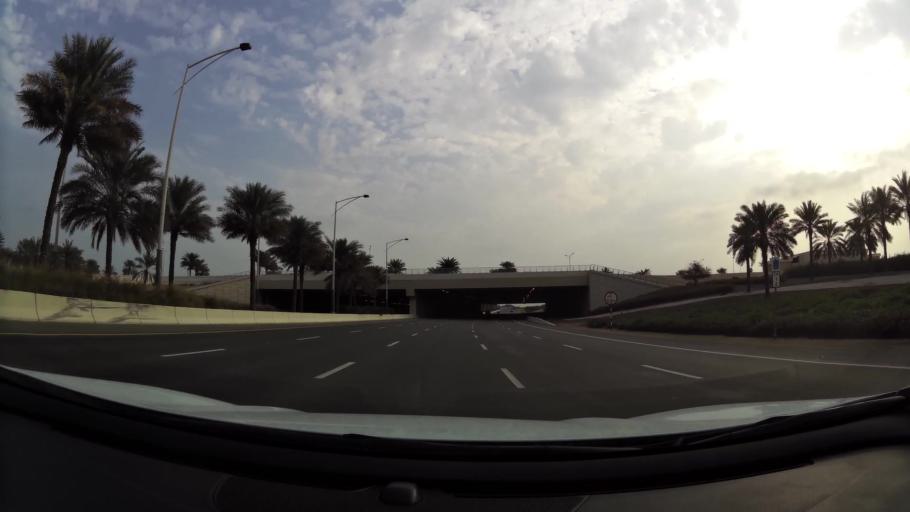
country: AE
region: Abu Dhabi
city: Abu Dhabi
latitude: 24.5416
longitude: 54.4407
